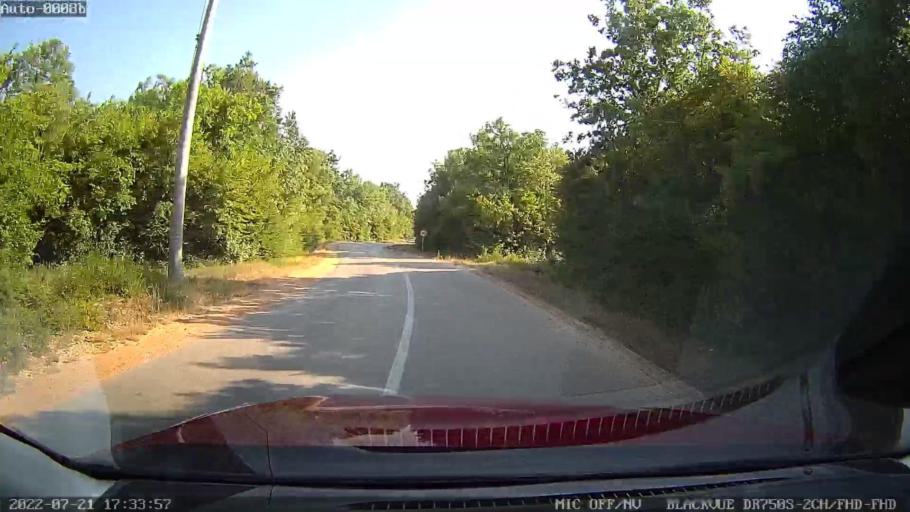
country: HR
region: Istarska
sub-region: Grad Rovinj
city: Rovinj
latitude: 45.1683
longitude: 13.7448
